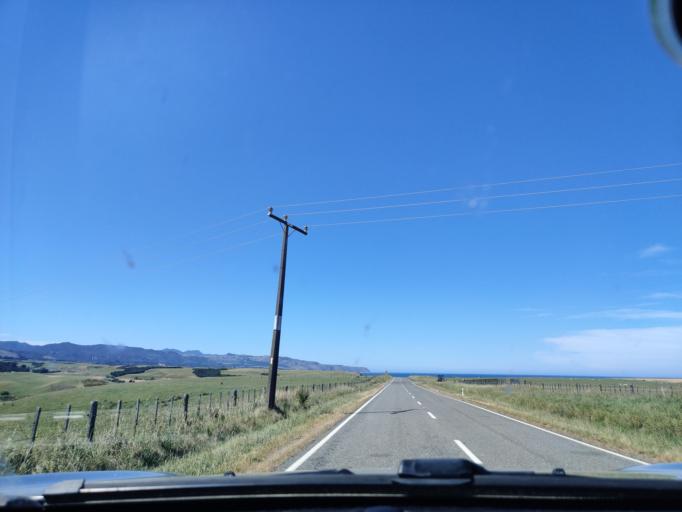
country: NZ
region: Wellington
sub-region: Upper Hutt City
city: Upper Hutt
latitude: -41.3939
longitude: 175.1764
